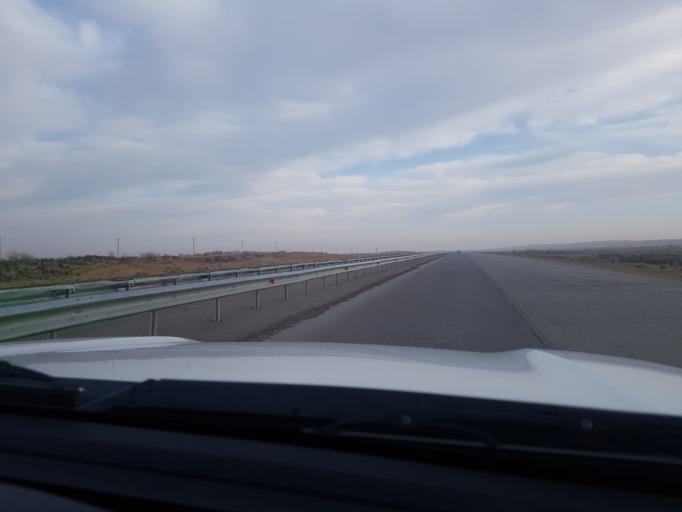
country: TM
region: Ahal
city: Abadan
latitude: 38.5317
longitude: 58.5105
